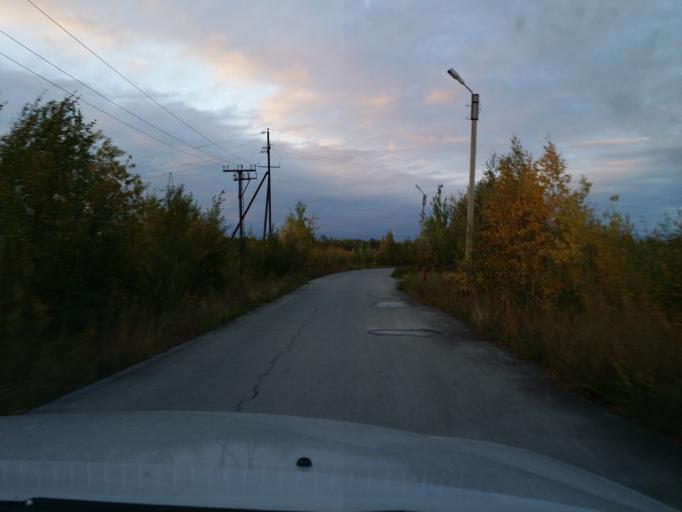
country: RU
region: Khanty-Mansiyskiy Avtonomnyy Okrug
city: Megion
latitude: 61.0825
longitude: 76.1597
